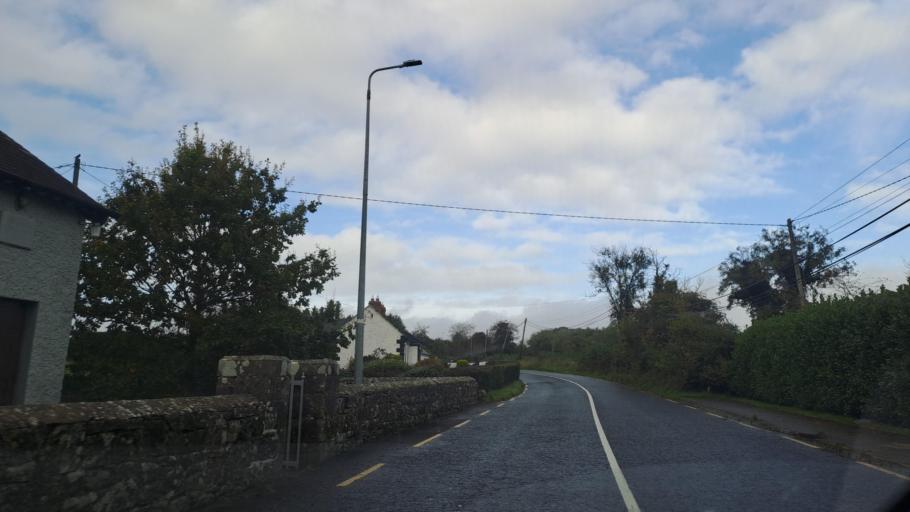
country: IE
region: Ulster
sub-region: County Monaghan
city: Carrickmacross
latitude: 53.9346
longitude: -6.7167
